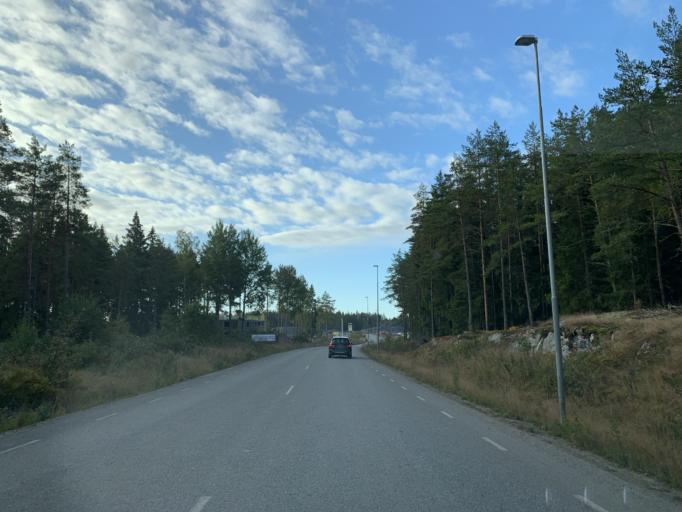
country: SE
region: Stockholm
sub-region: Upplands-Bro Kommun
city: Bro
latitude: 59.5091
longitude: 17.6152
